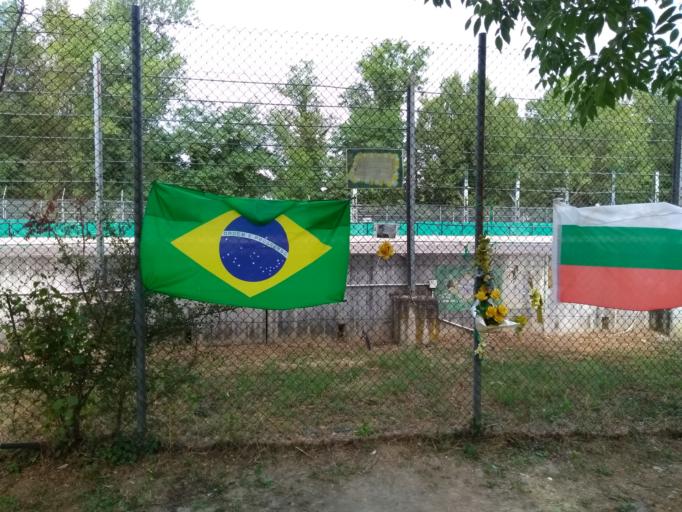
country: IT
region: Emilia-Romagna
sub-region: Provincia di Bologna
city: Imola
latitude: 44.3423
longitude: 11.7062
